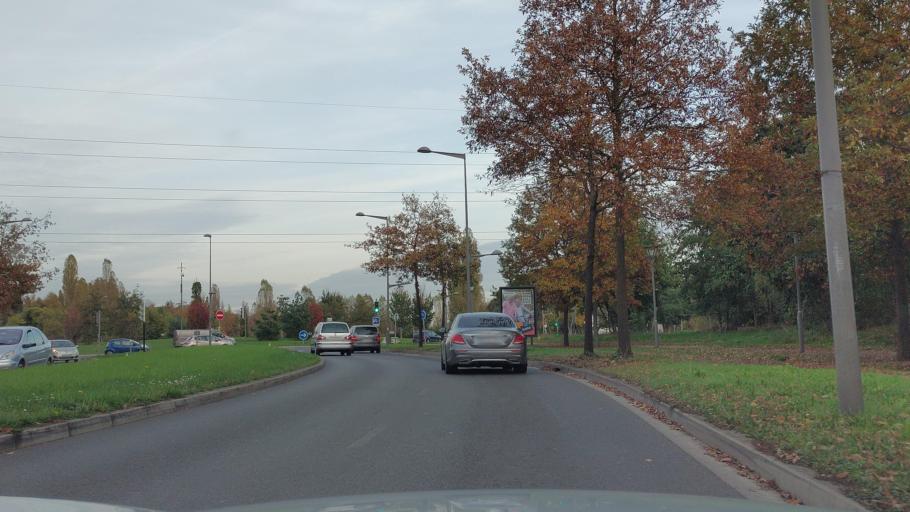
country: FR
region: Ile-de-France
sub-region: Departement de Seine-Saint-Denis
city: Aulnay-sous-Bois
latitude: 48.9539
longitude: 2.5079
